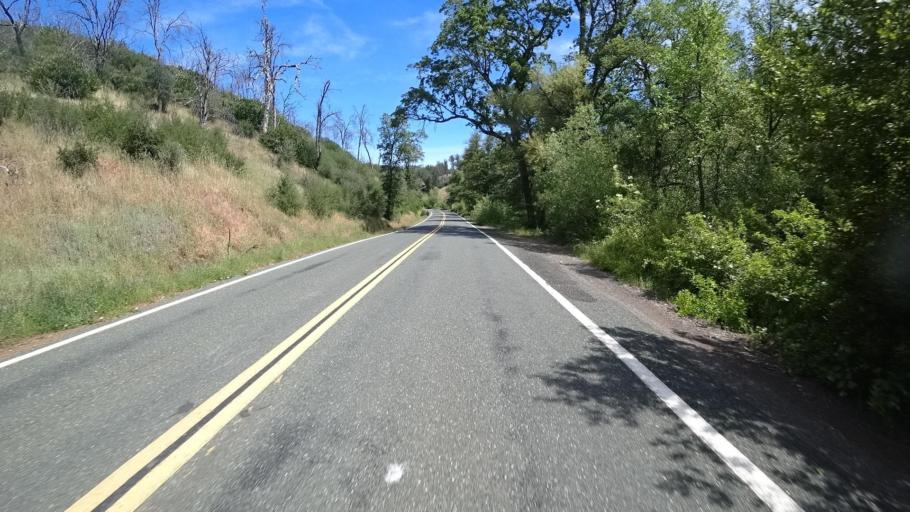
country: US
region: California
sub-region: Lake County
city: Lower Lake
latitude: 38.8886
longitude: -122.6656
